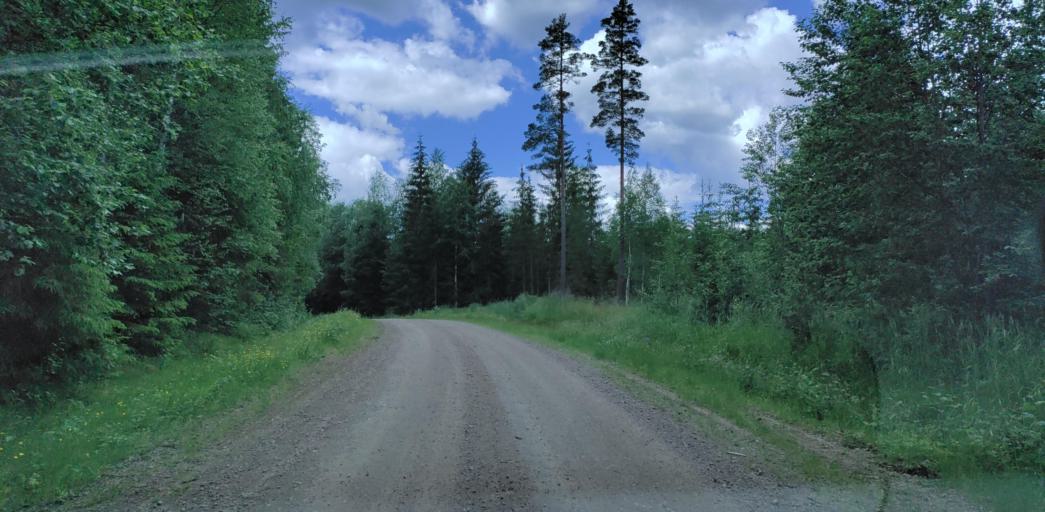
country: SE
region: Vaermland
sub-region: Hagfors Kommun
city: Ekshaerad
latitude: 60.0877
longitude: 13.4357
